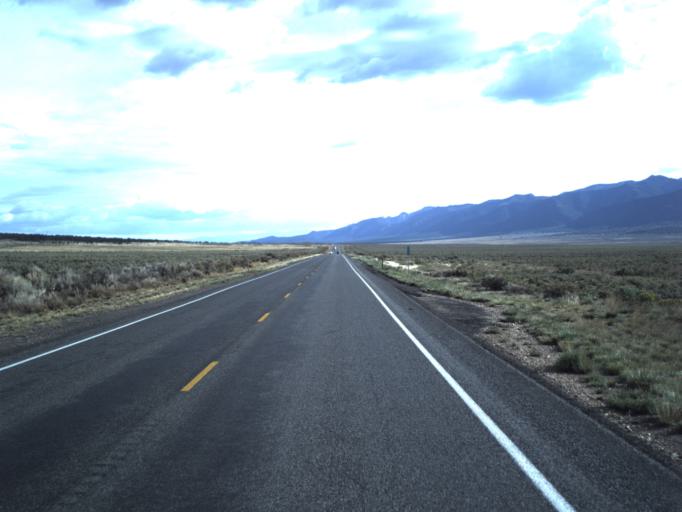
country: US
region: Utah
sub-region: Sevier County
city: Aurora
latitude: 39.0680
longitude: -112.0421
